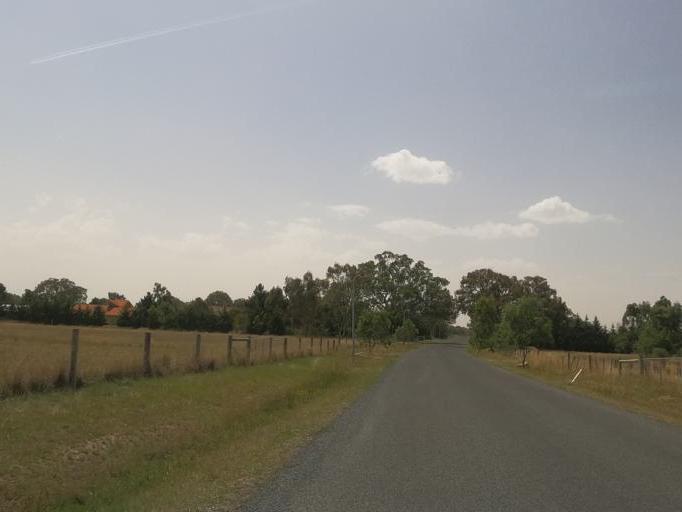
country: AU
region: Victoria
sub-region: Hume
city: Craigieburn
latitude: -37.5598
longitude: 144.8974
